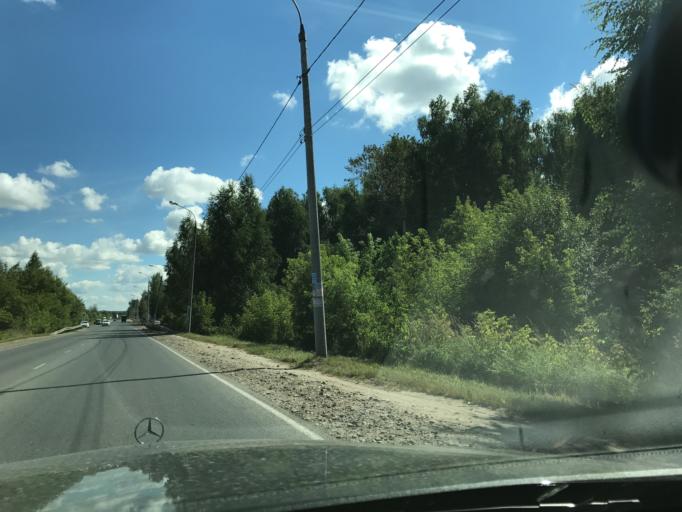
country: RU
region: Nizjnij Novgorod
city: Gorbatovka
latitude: 56.2152
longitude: 43.7593
